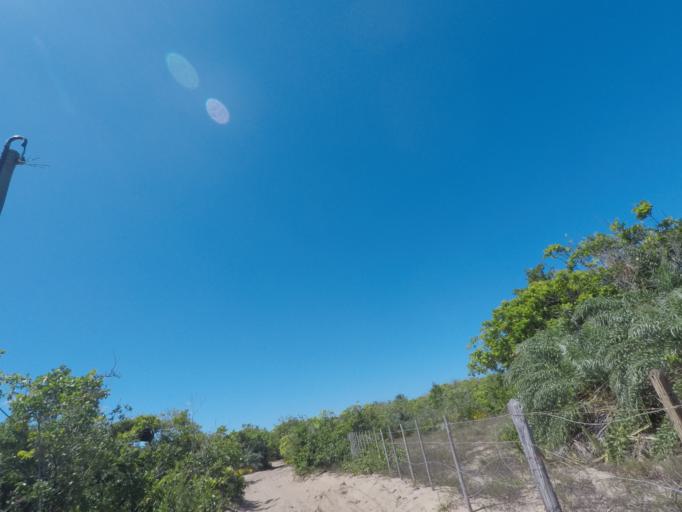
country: BR
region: Bahia
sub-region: Marau
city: Marau
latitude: -13.9566
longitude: -38.9344
